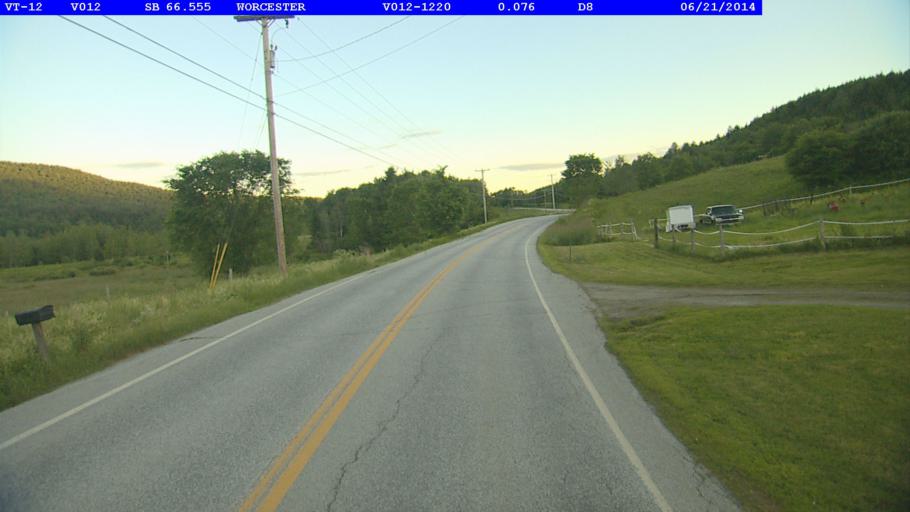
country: US
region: Vermont
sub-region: Washington County
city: Montpelier
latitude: 44.3537
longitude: -72.5646
